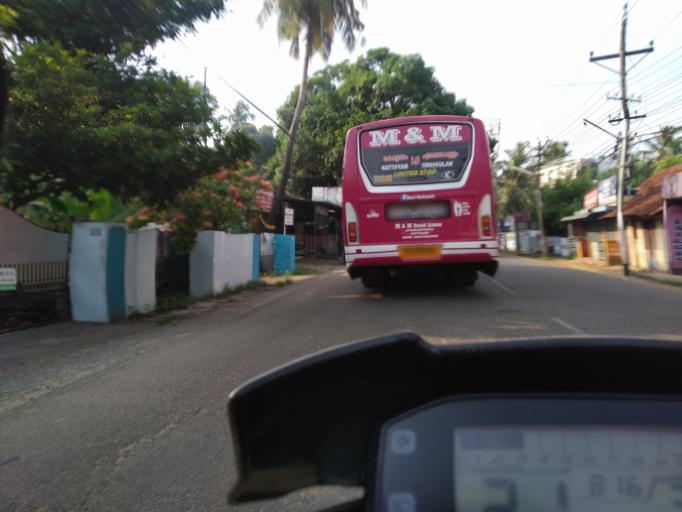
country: IN
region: Kerala
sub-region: Alappuzha
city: Arukutti
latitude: 9.9383
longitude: 76.3517
